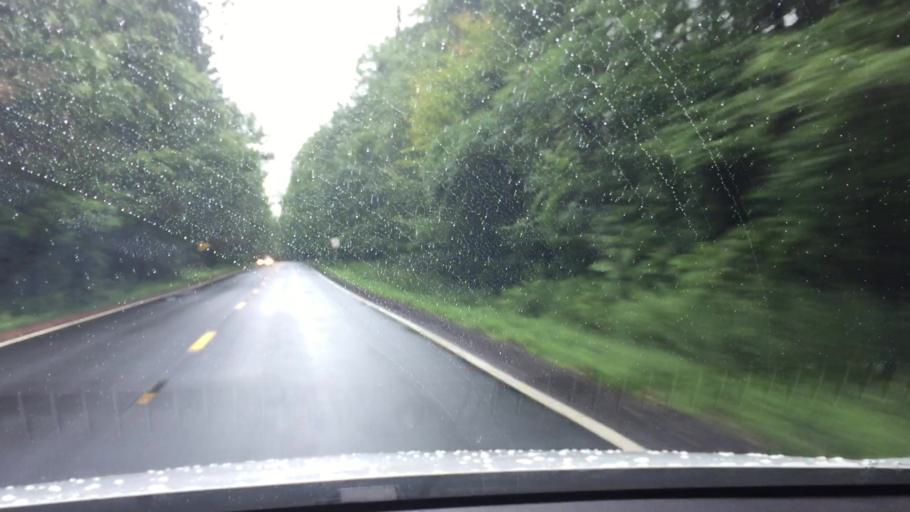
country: US
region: Massachusetts
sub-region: Berkshire County
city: Hinsdale
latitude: 42.4009
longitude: -73.1722
